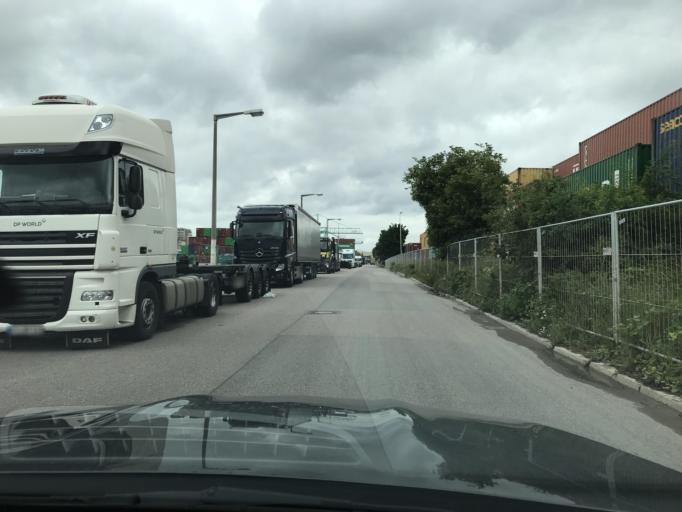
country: DE
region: Baden-Wuerttemberg
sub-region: Regierungsbezirk Stuttgart
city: Ostfildern
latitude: 48.7656
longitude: 9.2613
